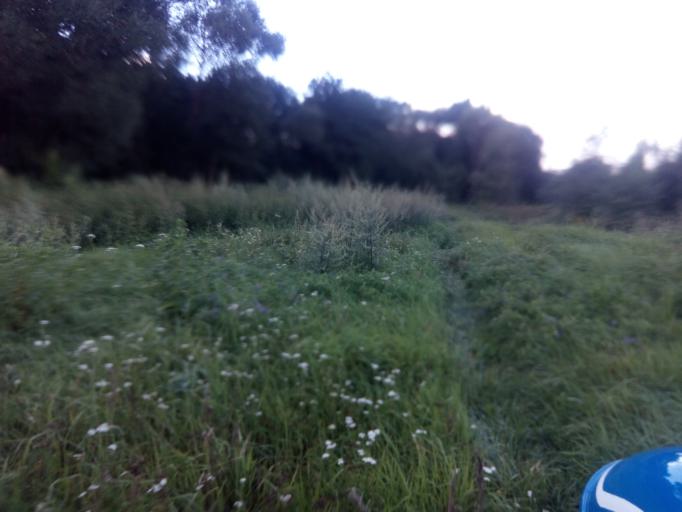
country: BY
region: Vitebsk
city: Dzisna
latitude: 55.6786
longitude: 28.3172
